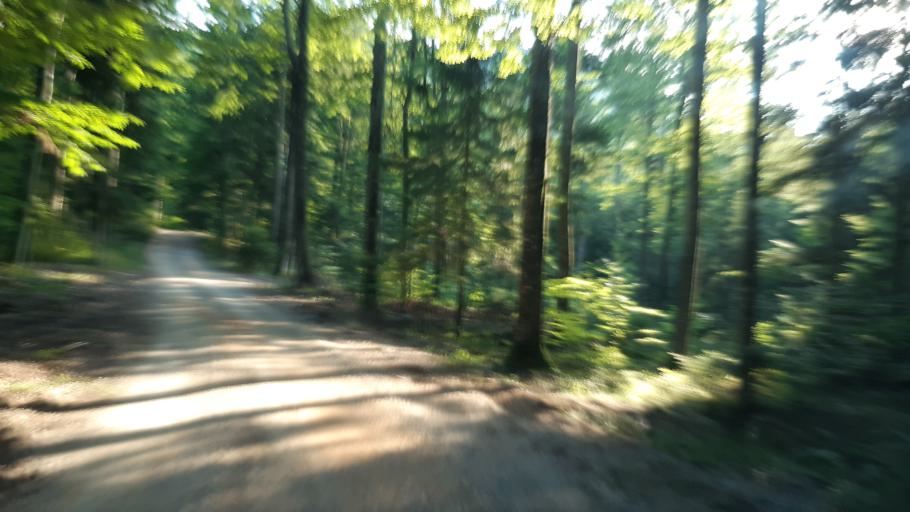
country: SI
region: Dolenjske Toplice
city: Dolenjske Toplice
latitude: 45.6921
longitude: 15.0065
